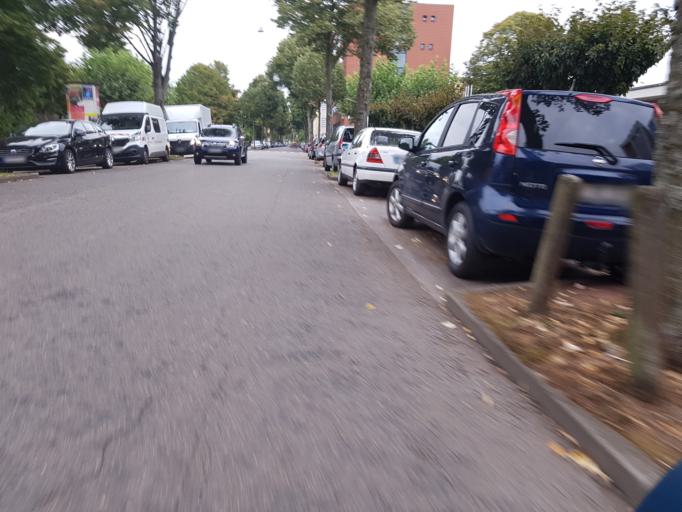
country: DE
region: Saarland
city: Saarbrucken
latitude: 49.2349
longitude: 6.9778
